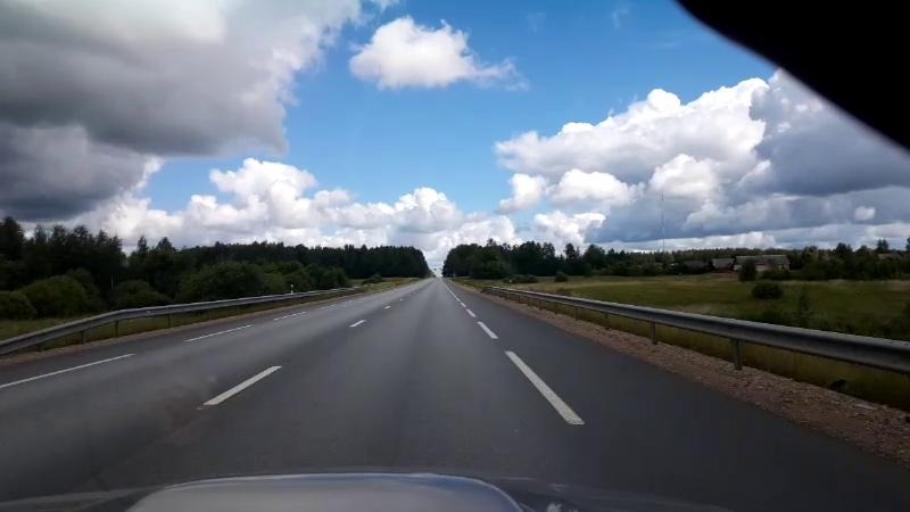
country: LV
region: Lecava
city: Iecava
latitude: 56.6604
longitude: 24.2322
